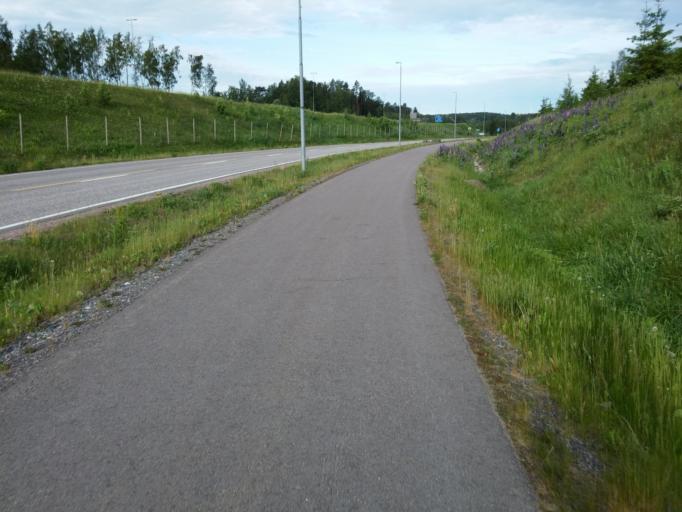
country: FI
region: Uusimaa
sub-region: Helsinki
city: Kirkkonummi
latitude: 60.1373
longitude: 24.5278
